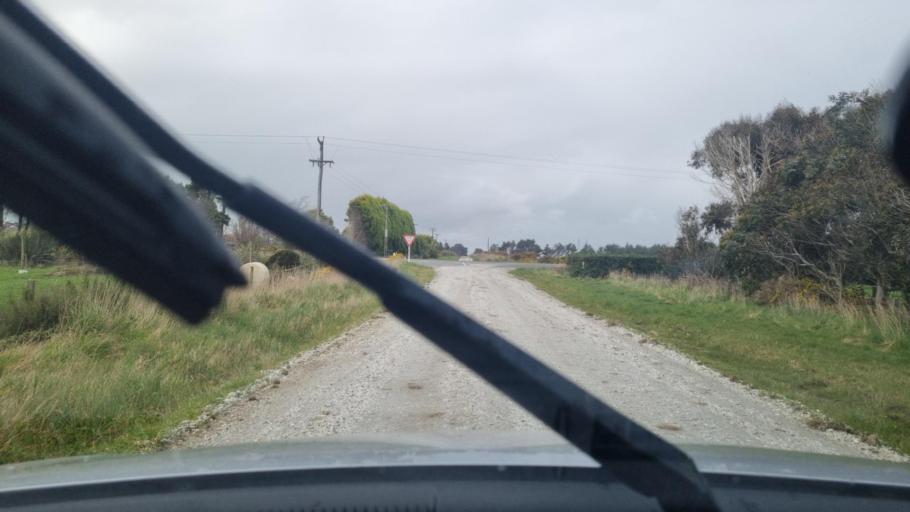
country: NZ
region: Southland
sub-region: Invercargill City
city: Invercargill
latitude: -46.4965
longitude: 168.4184
